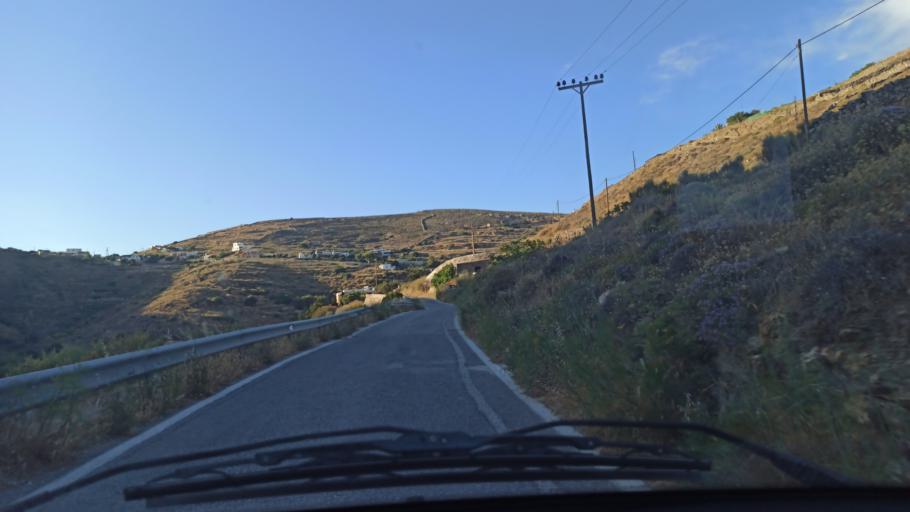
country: GR
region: South Aegean
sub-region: Nomos Kykladon
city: Ano Syros
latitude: 37.4585
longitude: 24.9314
